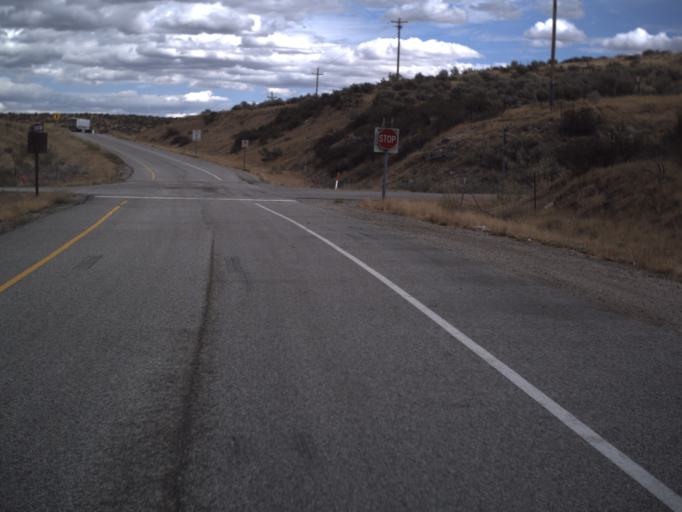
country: US
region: Utah
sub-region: Box Elder County
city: Garland
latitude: 41.8965
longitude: -112.5452
